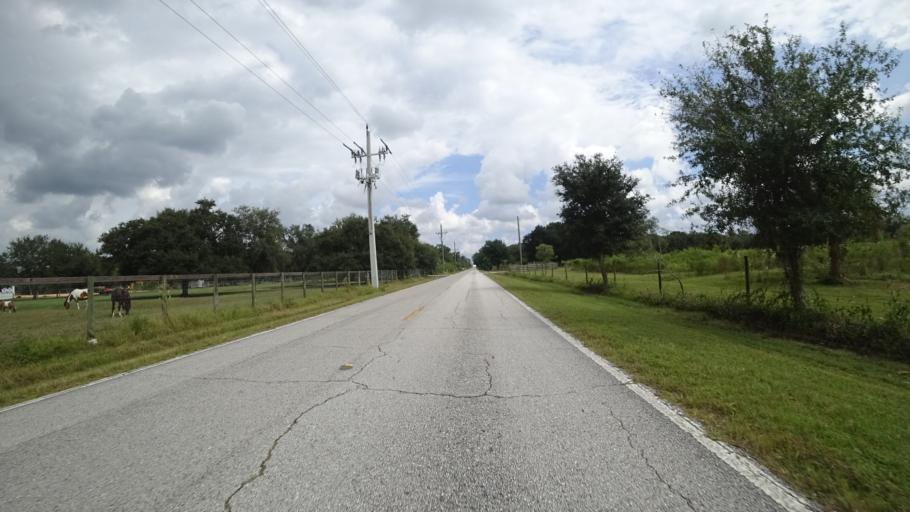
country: US
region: Florida
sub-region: Manatee County
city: Ellenton
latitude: 27.4878
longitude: -82.3784
